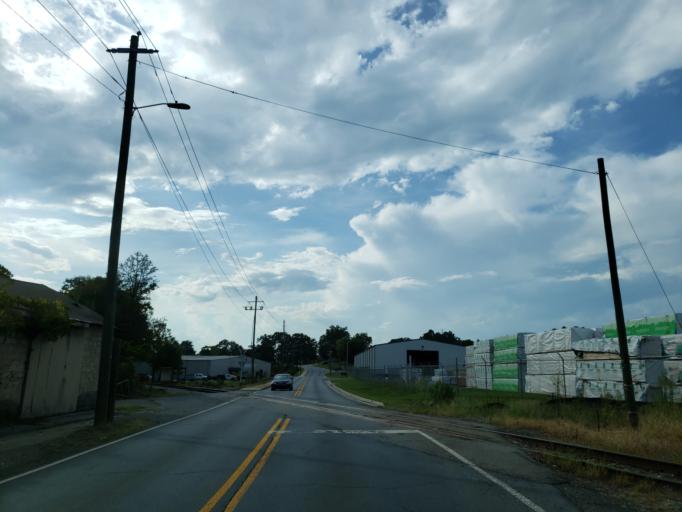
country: US
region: Georgia
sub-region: Bartow County
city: Cartersville
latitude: 34.1747
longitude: -84.8027
